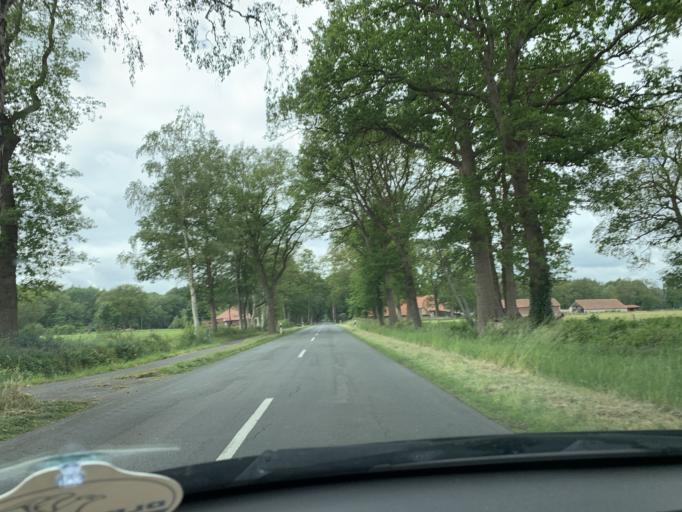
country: DE
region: Lower Saxony
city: Bockhorn
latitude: 53.3513
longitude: 8.0552
